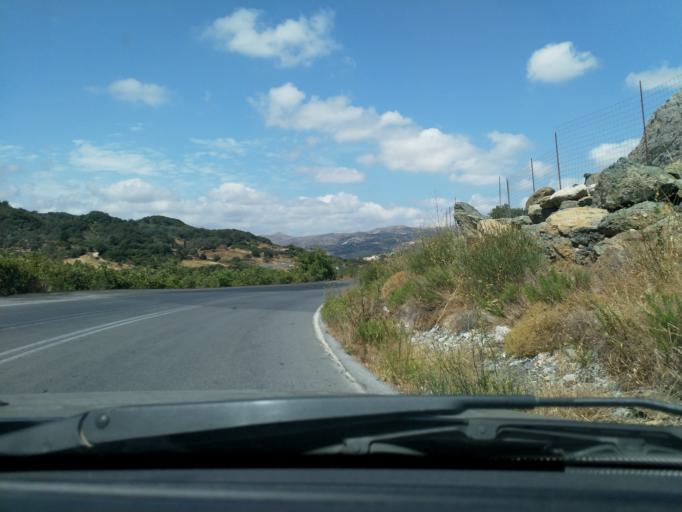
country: GR
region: Crete
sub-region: Nomos Rethymnis
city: Agia Foteini
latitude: 35.1984
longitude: 24.5444
